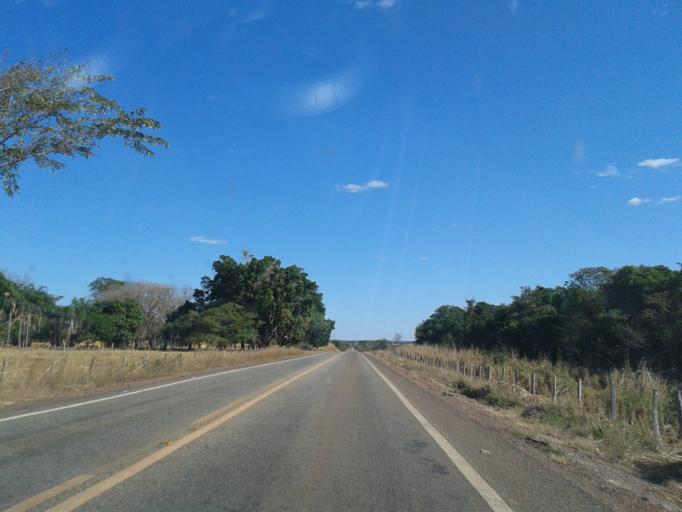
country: BR
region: Goias
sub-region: Mozarlandia
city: Mozarlandia
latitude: -14.5555
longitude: -50.4952
